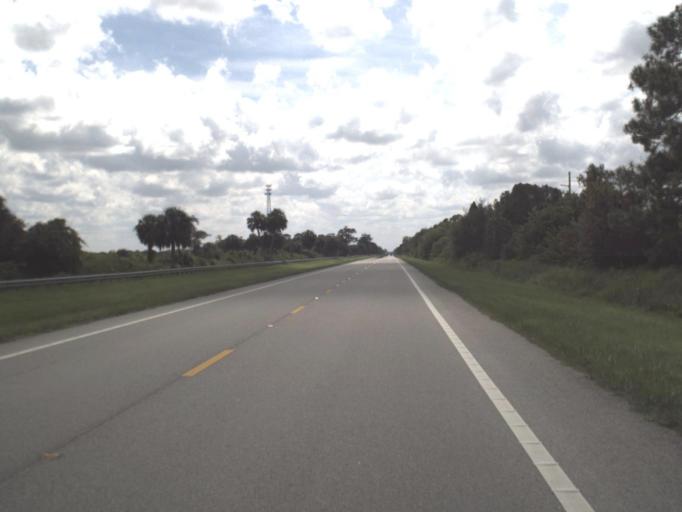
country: US
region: Florida
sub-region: Collier County
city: Immokalee
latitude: 26.3233
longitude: -81.3431
